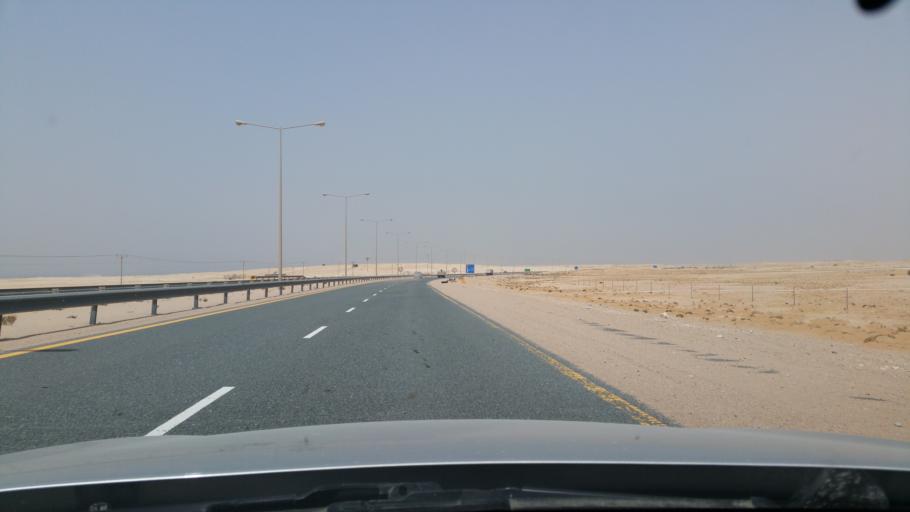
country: QA
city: Umm Bab
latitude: 25.1377
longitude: 50.8327
